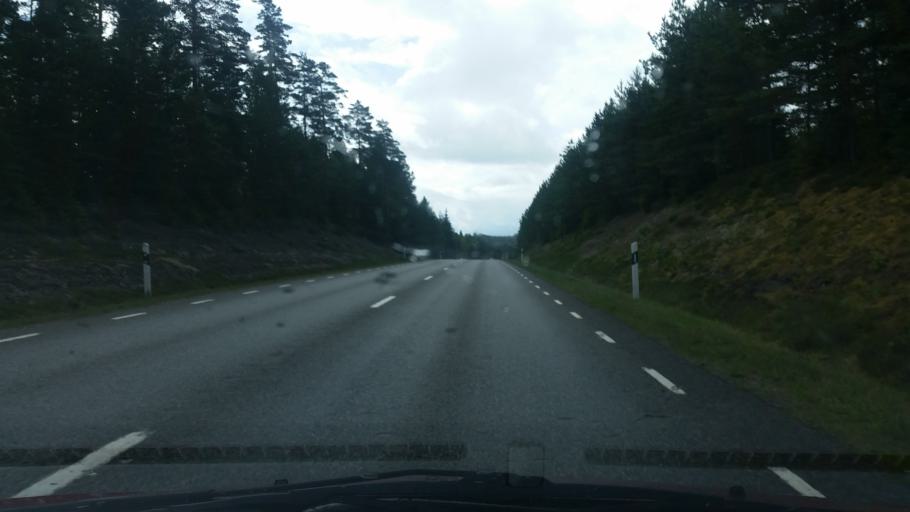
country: SE
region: Joenkoeping
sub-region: Mullsjo Kommun
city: Mullsjoe
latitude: 57.6885
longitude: 13.8480
